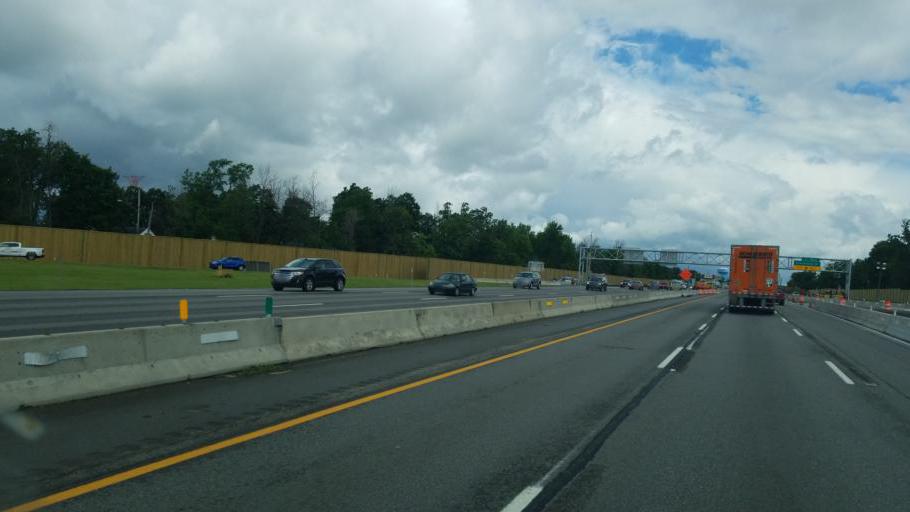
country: US
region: New York
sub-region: Erie County
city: Cheektowaga
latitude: 42.9350
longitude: -78.7662
